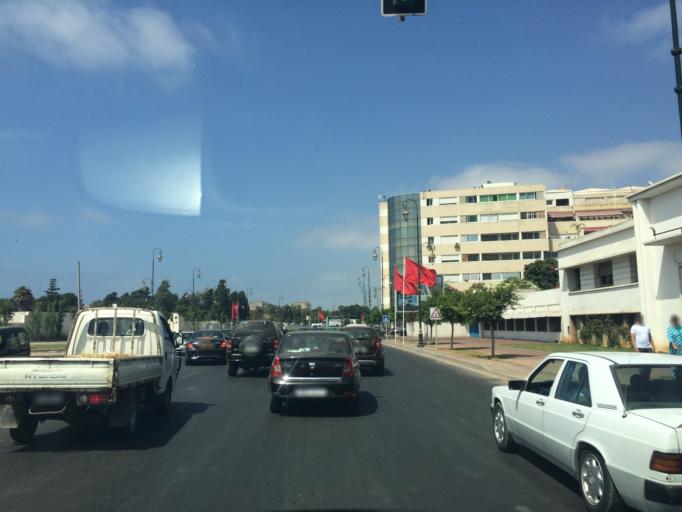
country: MA
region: Rabat-Sale-Zemmour-Zaer
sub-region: Rabat
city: Rabat
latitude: 34.0025
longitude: -6.8593
